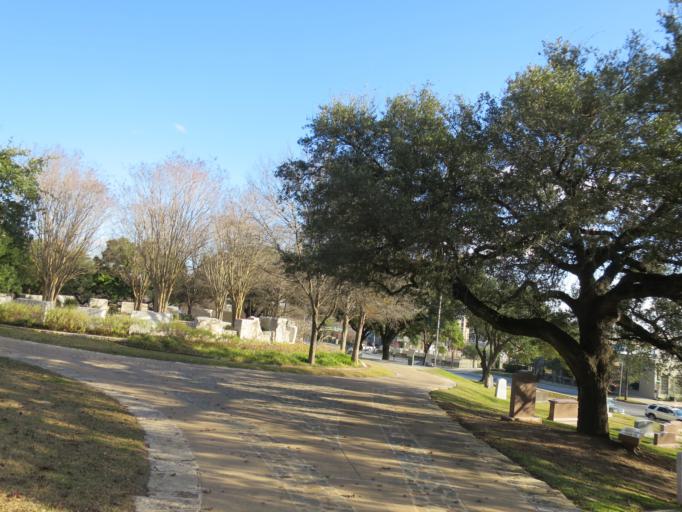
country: US
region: Texas
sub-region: Travis County
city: Austin
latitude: 30.2650
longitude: -97.7272
